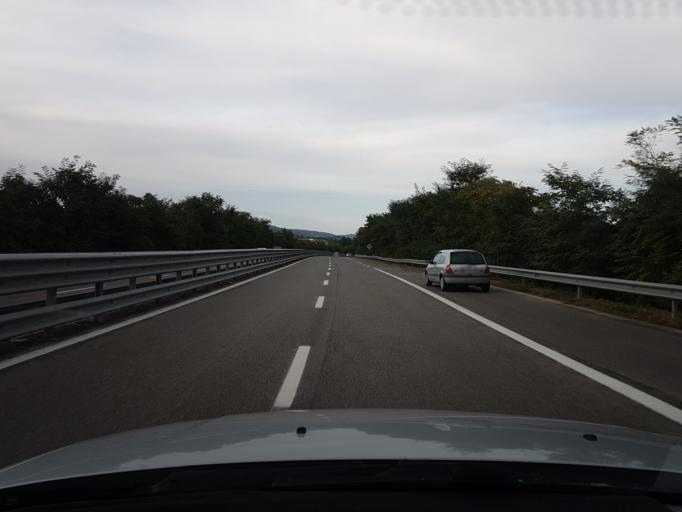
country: IT
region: Sardinia
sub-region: Provincia di Nuoro
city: Nuoro
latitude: 40.3239
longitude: 9.2808
